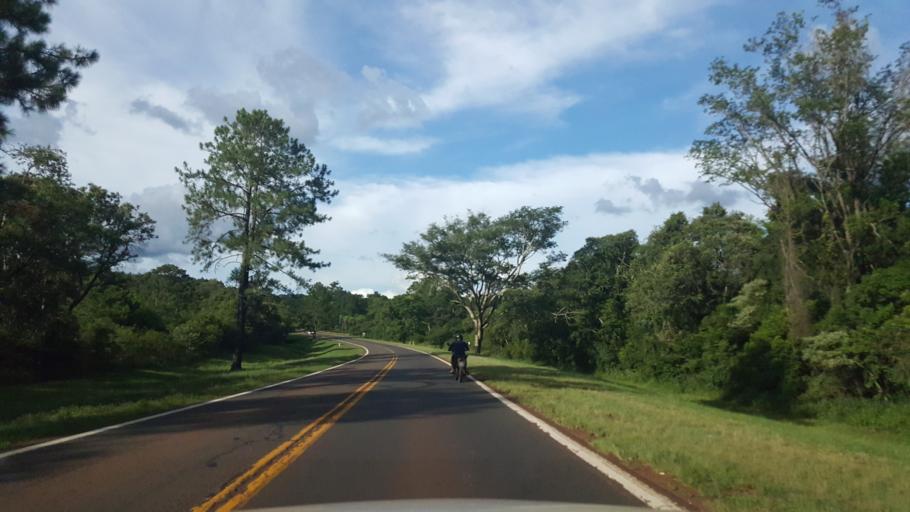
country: AR
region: Misiones
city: Santa Ana
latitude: -27.3645
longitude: -55.5583
